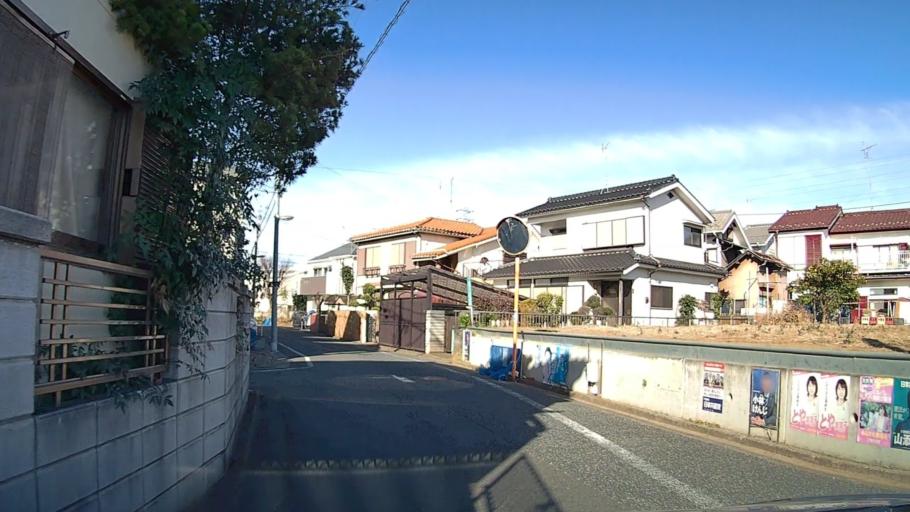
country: JP
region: Saitama
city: Wako
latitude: 35.7587
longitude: 139.6121
